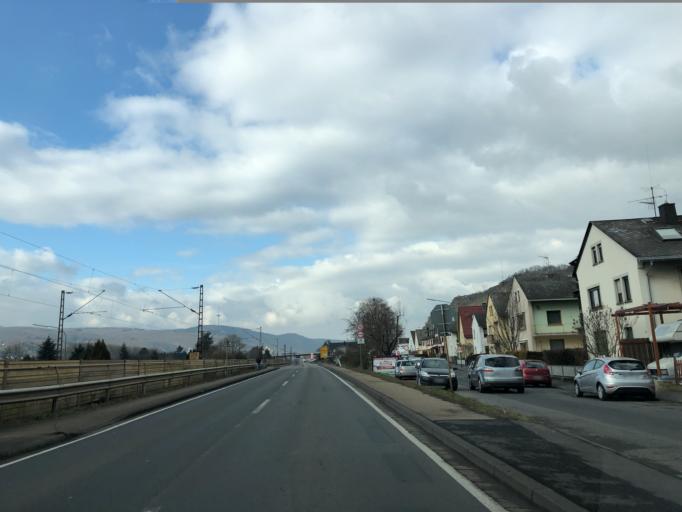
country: DE
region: Rheinland-Pfalz
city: Braubach
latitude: 50.2816
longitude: 7.6344
